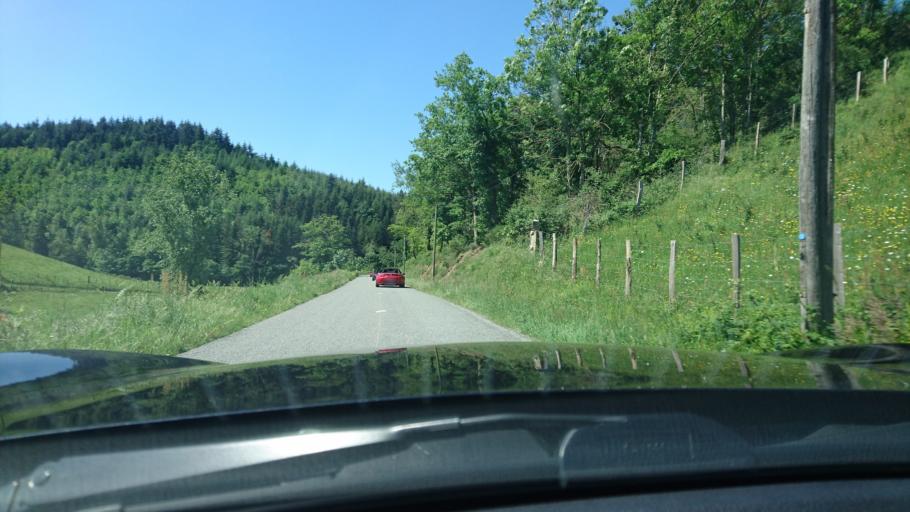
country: FR
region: Rhone-Alpes
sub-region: Departement de la Loire
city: Bussieres
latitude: 45.8824
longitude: 4.2982
